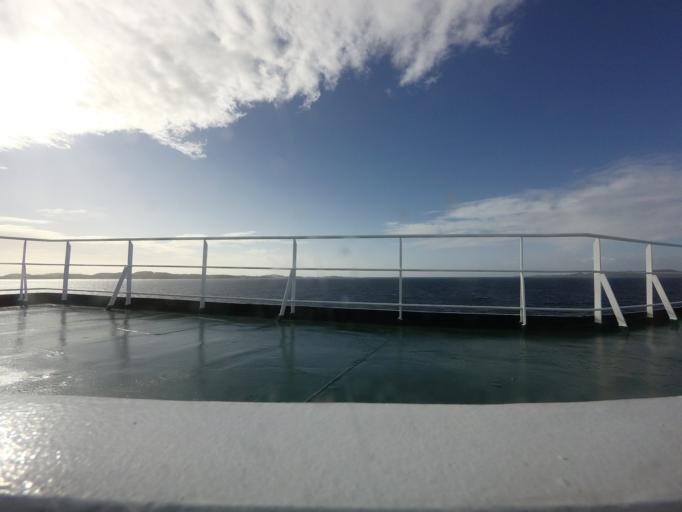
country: NO
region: Sogn og Fjordane
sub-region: Solund
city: Hardbakke
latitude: 61.0148
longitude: 4.8451
